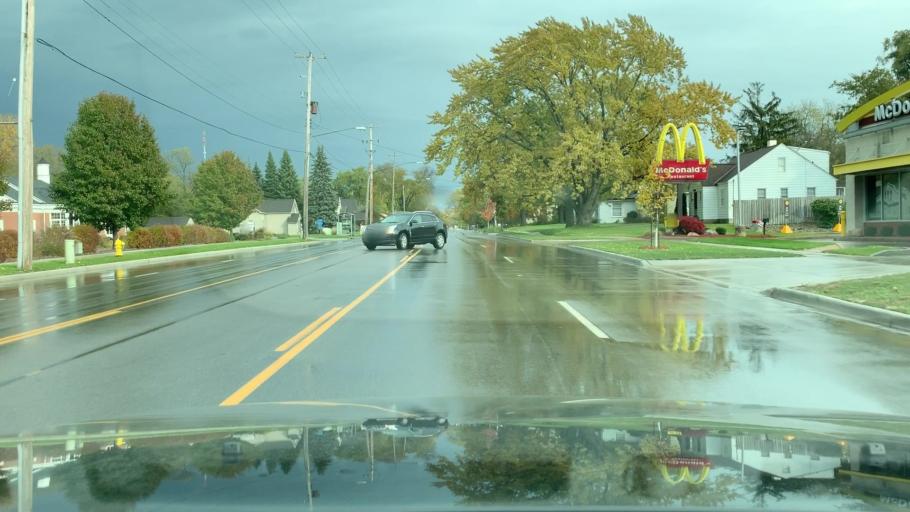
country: US
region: Michigan
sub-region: Kent County
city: Grand Rapids
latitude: 42.9844
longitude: -85.6381
